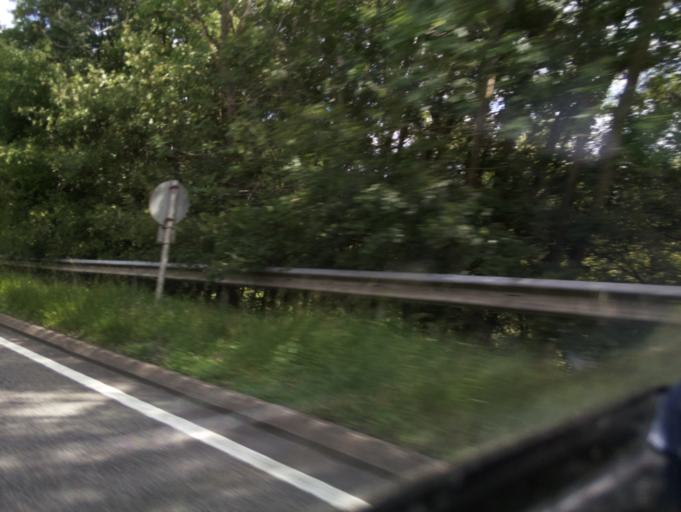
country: GB
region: England
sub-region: Oxfordshire
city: Boars Hill
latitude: 51.7409
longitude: -1.3253
